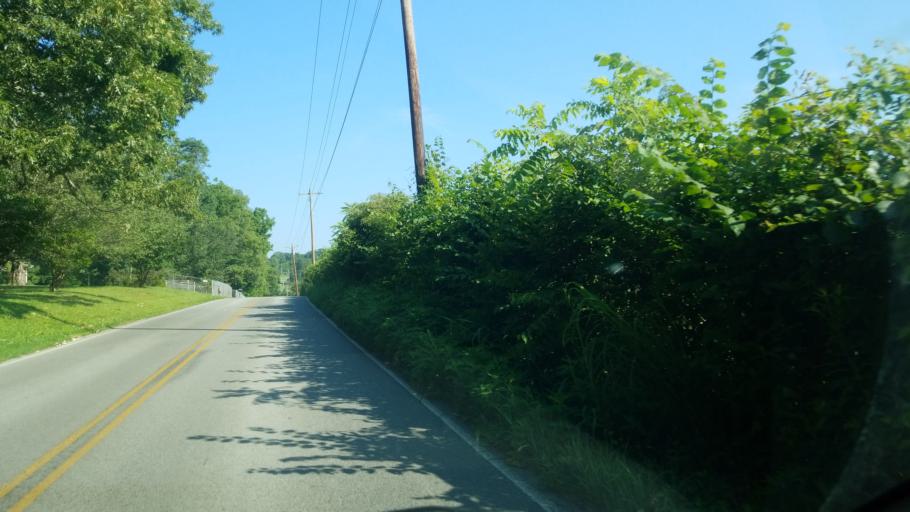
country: US
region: Tennessee
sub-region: Loudon County
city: Loudon
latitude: 35.7795
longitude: -84.3548
